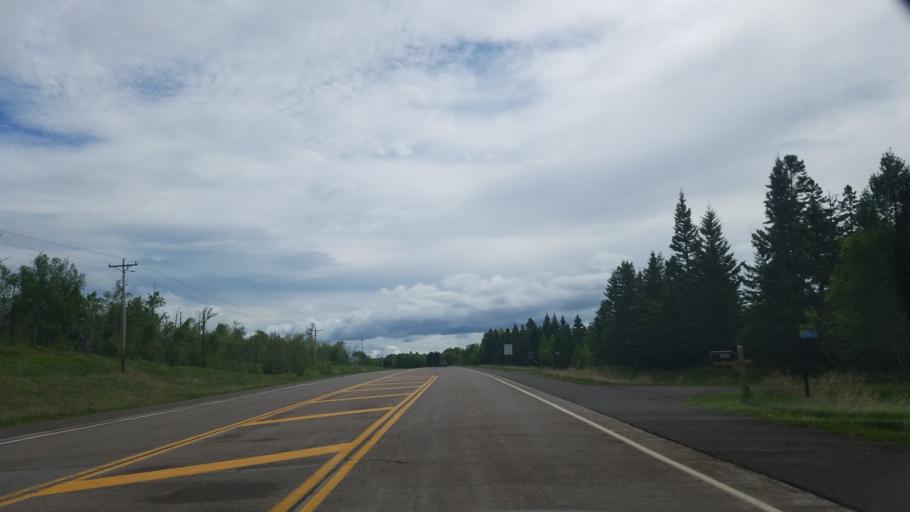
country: US
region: Minnesota
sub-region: Lake County
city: Two Harbors
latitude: 47.1228
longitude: -91.4993
